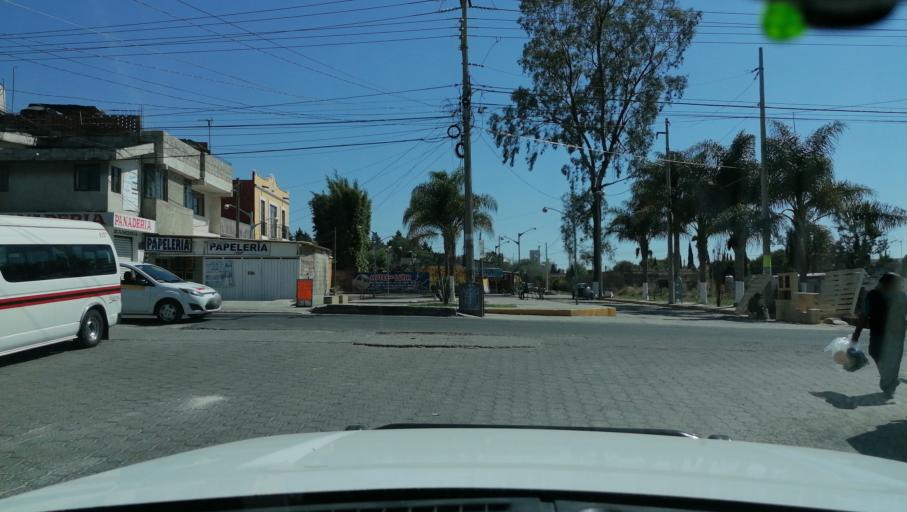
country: MX
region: Tlaxcala
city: Tenancingo
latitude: 19.1509
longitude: -98.2201
